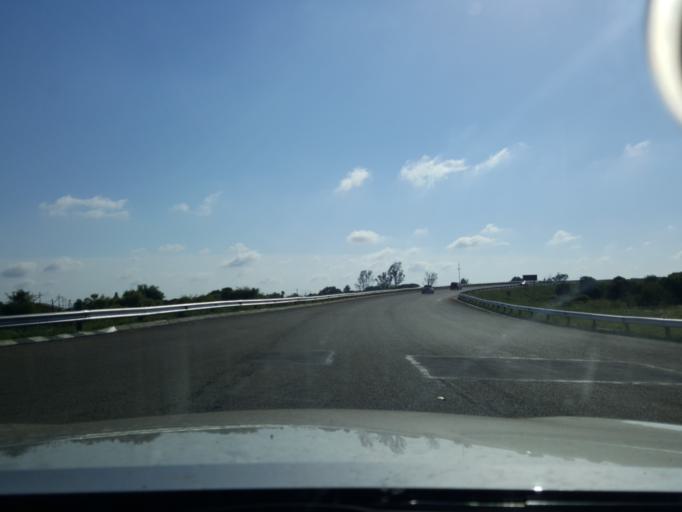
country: ZA
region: North-West
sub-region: Ngaka Modiri Molema District Municipality
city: Zeerust
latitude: -25.7545
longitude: 25.9580
